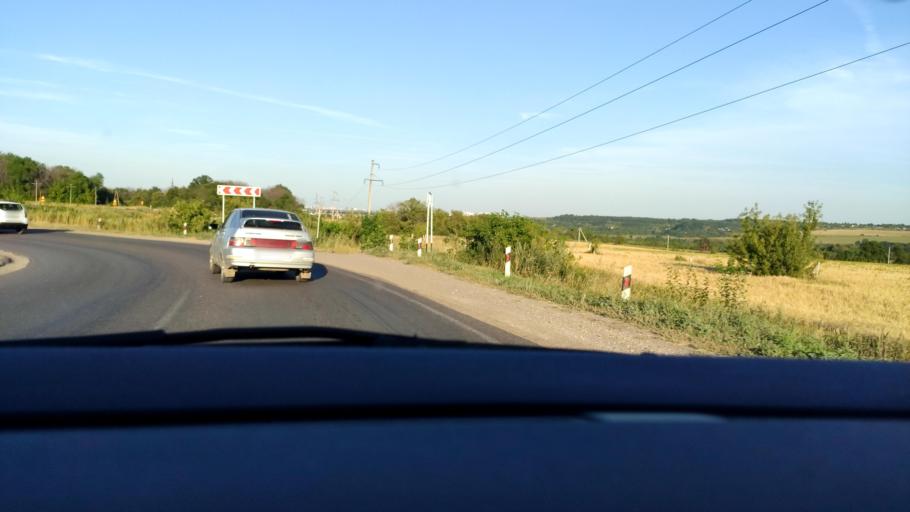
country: RU
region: Voronezj
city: Semiluki
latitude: 51.6833
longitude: 38.9767
